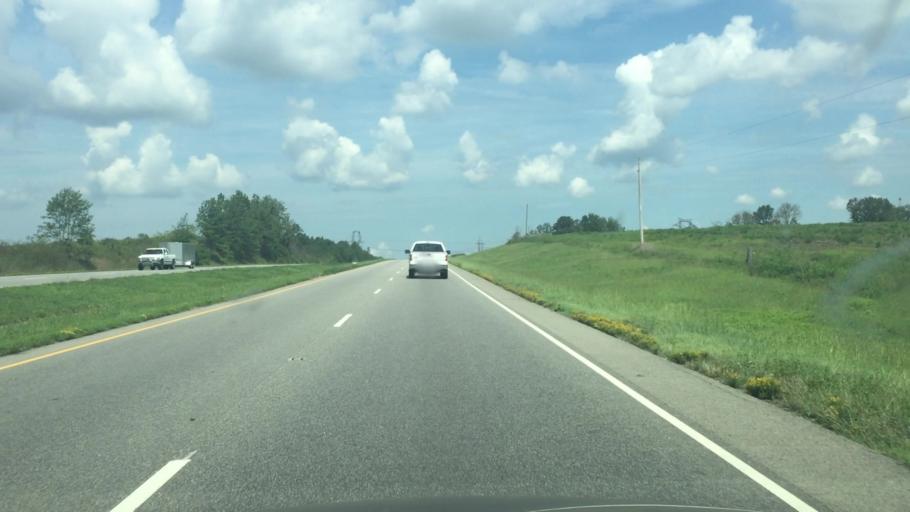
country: US
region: North Carolina
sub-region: Scotland County
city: Laurel Hill
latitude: 34.8476
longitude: -79.6130
